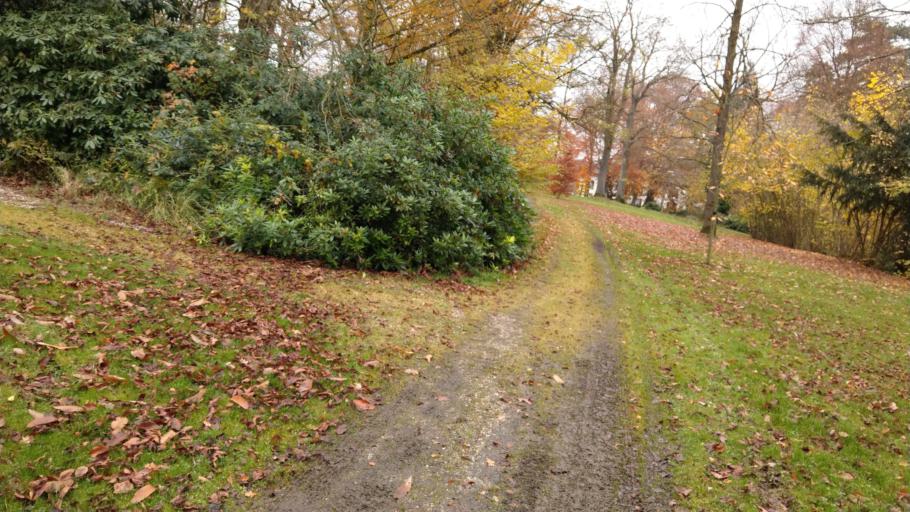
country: NL
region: Limburg
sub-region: Gemeente Vaals
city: Vaals
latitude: 50.7660
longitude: 5.9928
